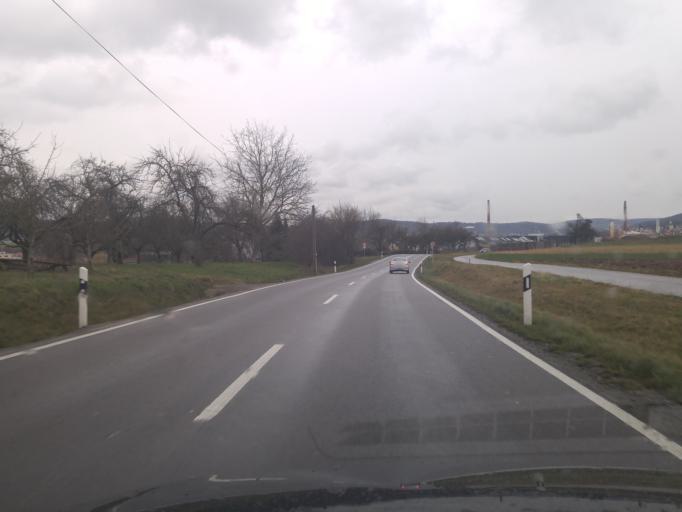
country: DE
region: Baden-Wuerttemberg
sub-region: Regierungsbezirk Stuttgart
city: Leutenbach
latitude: 48.8862
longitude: 9.3818
